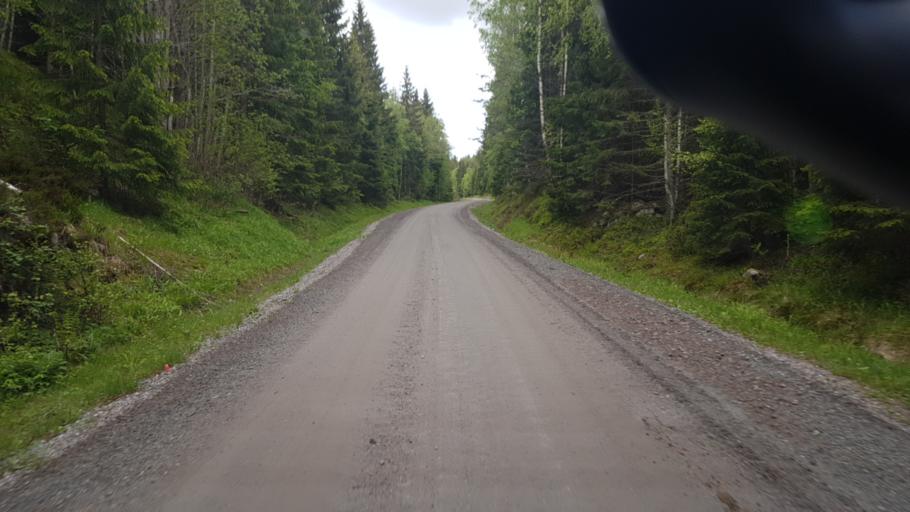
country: NO
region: Ostfold
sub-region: Romskog
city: Romskog
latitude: 59.7155
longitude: 11.9984
